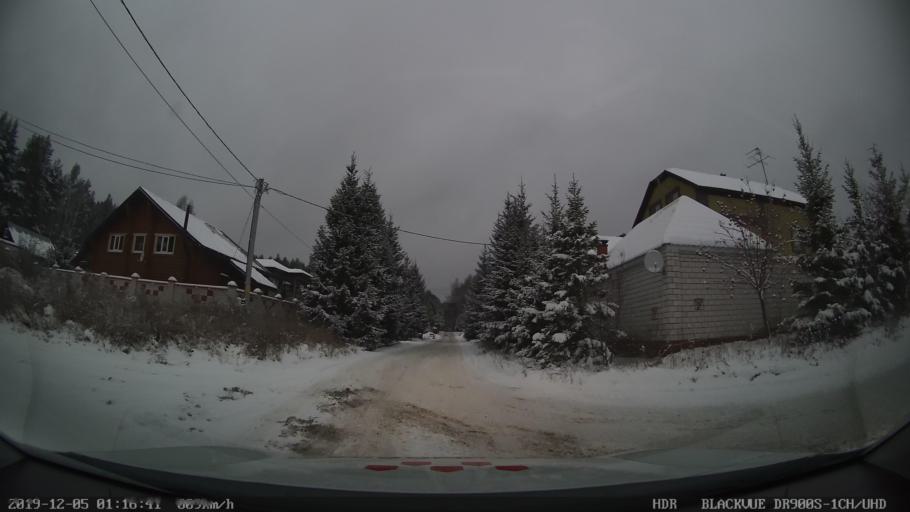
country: RU
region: Tatarstan
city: Stolbishchi
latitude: 55.6473
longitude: 49.1105
